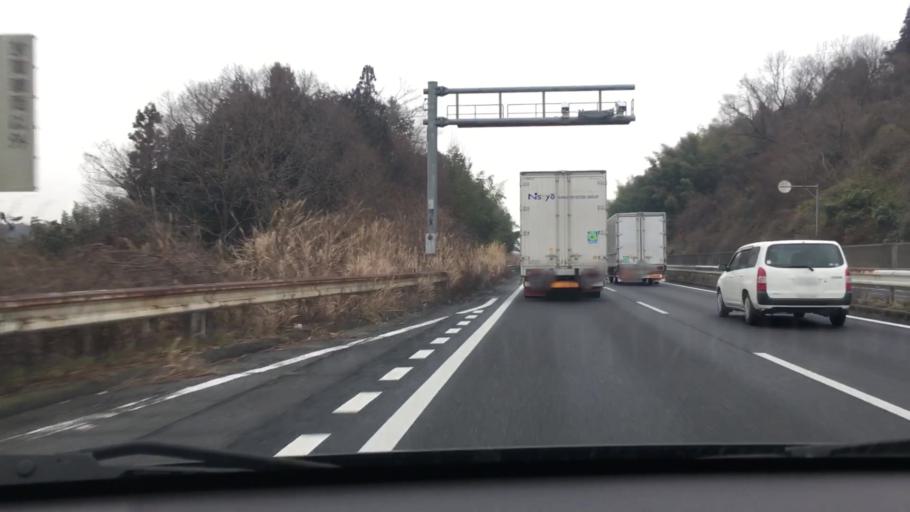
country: JP
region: Mie
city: Ueno-ebisumachi
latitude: 34.7033
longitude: 136.0695
